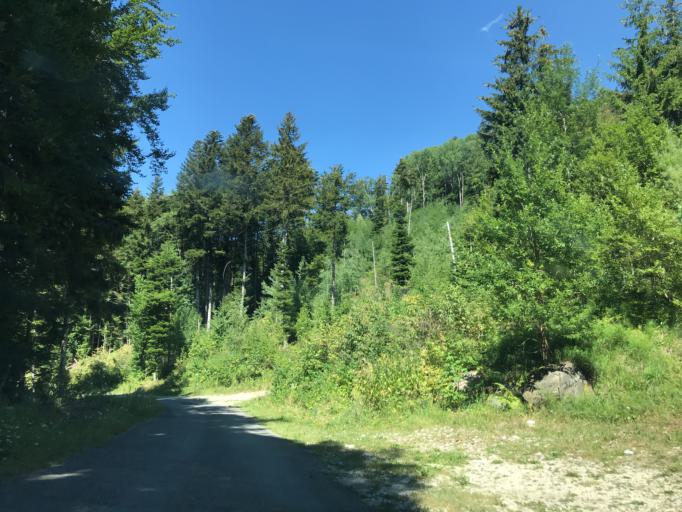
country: FR
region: Rhone-Alpes
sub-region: Departement de la Haute-Savoie
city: Thorens-Glieres
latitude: 45.9714
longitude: 6.2333
